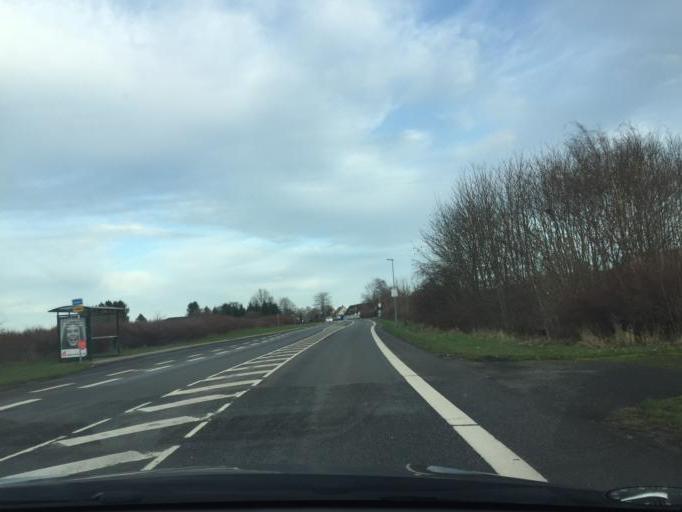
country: DK
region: South Denmark
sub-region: Faaborg-Midtfyn Kommune
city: Ringe
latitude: 55.2277
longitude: 10.4640
